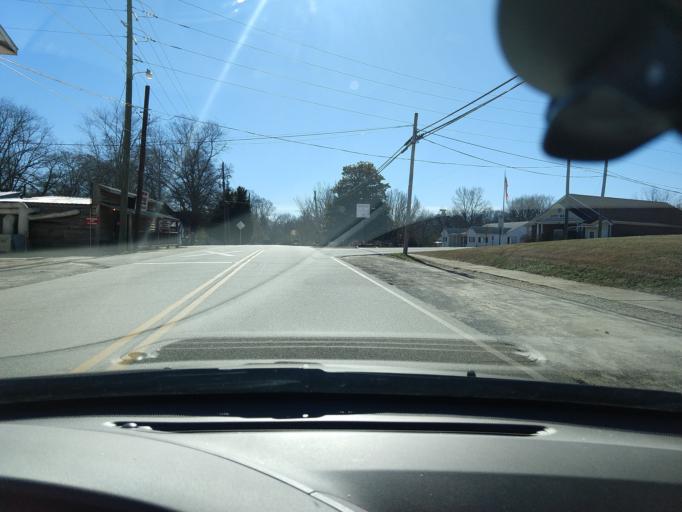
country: US
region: Georgia
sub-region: Walton County
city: Social Circle
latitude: 33.5176
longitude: -83.7341
